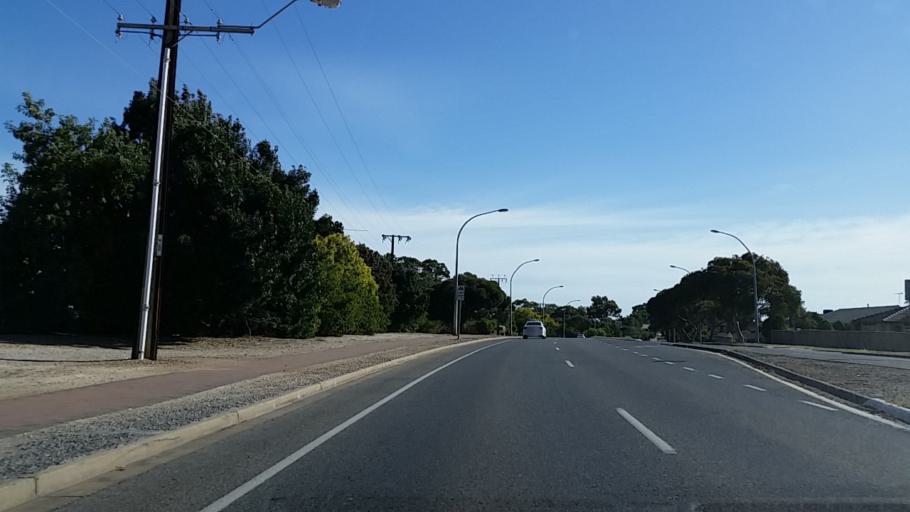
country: AU
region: South Australia
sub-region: Tea Tree Gully
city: Hope Valley
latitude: -34.8514
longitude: 138.7117
